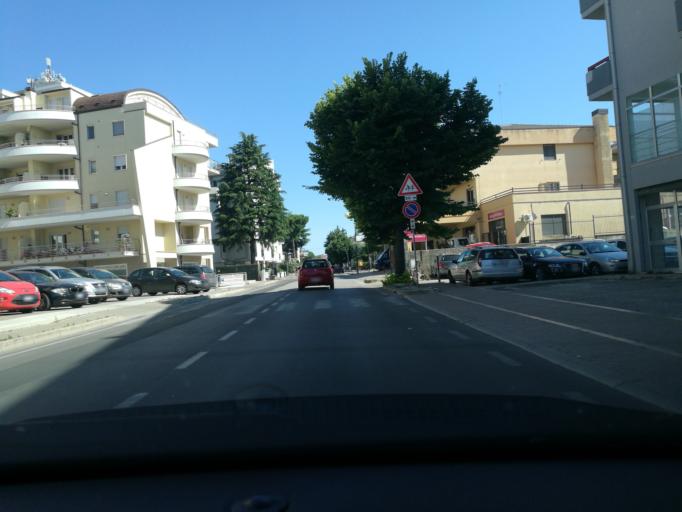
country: IT
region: Abruzzo
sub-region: Provincia di Chieti
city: Vasto
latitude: 42.1266
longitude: 14.7027
